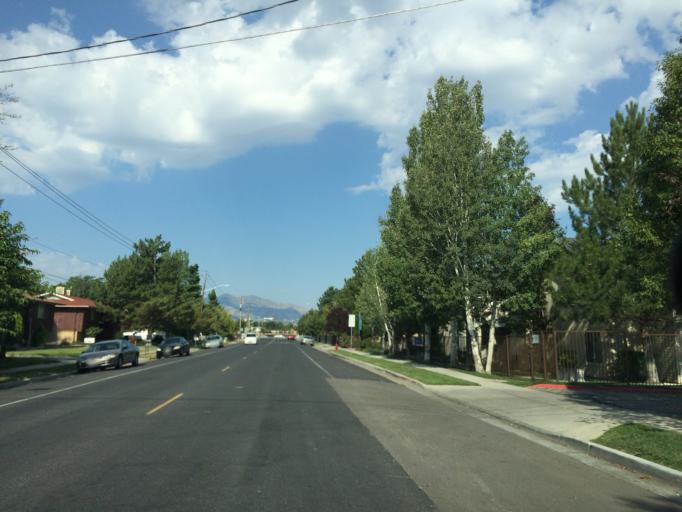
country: US
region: Utah
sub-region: Salt Lake County
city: West Valley City
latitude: 40.6929
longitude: -111.9744
